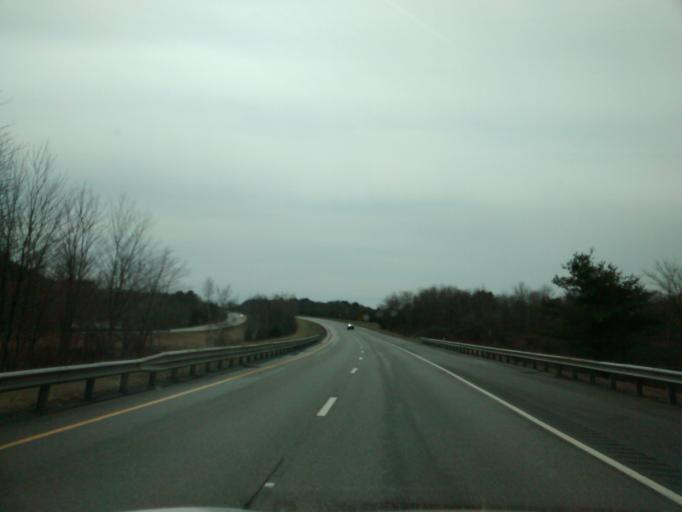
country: US
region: Massachusetts
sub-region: Worcester County
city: Oxford
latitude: 42.1504
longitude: -71.8574
